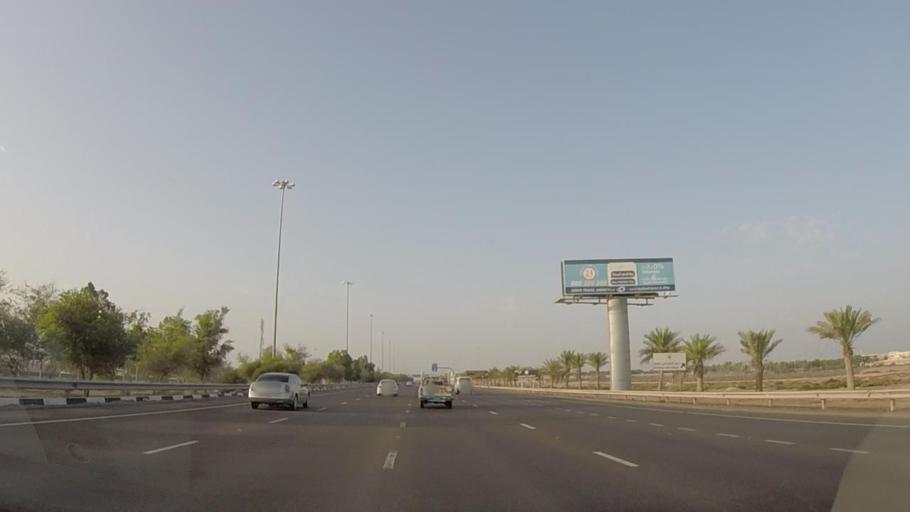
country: AE
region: Dubai
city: Dubai
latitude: 24.8651
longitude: 54.9114
